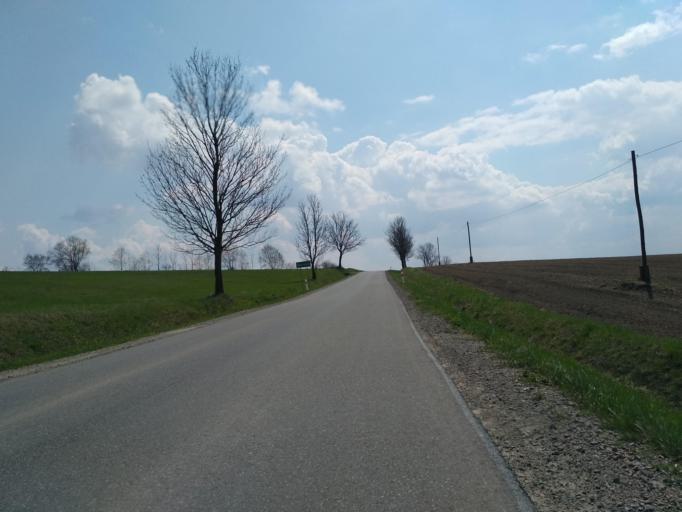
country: PL
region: Subcarpathian Voivodeship
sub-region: Powiat sanocki
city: Bukowsko
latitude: 49.4969
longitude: 22.0413
